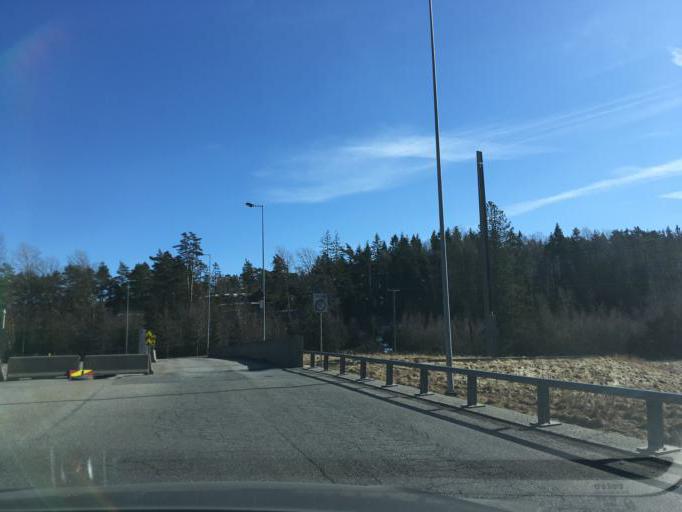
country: NO
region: Ostfold
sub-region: Halden
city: Halden
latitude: 59.1078
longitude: 11.2626
